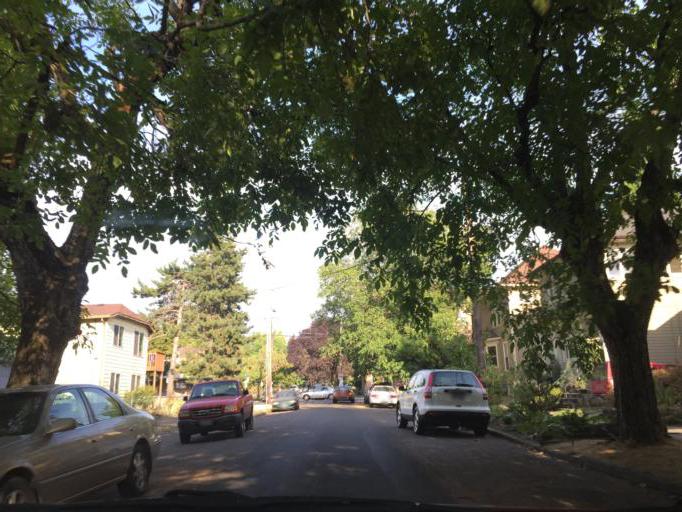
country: US
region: Oregon
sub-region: Multnomah County
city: Portland
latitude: 45.5250
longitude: -122.6381
